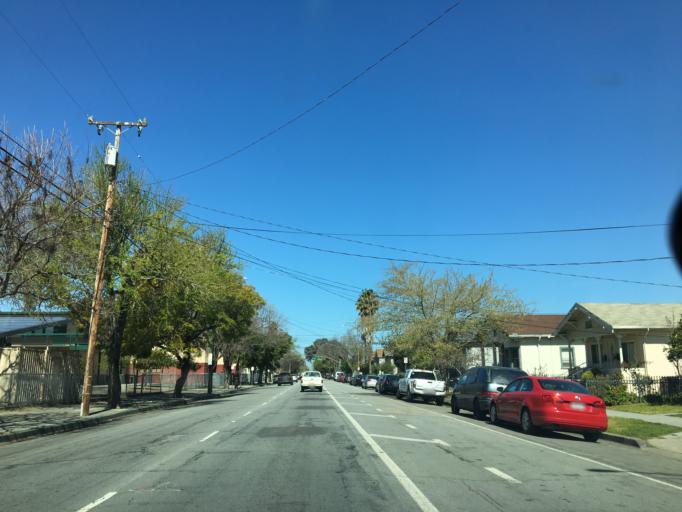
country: US
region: California
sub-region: Santa Clara County
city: San Jose
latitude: 37.3506
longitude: -121.8870
